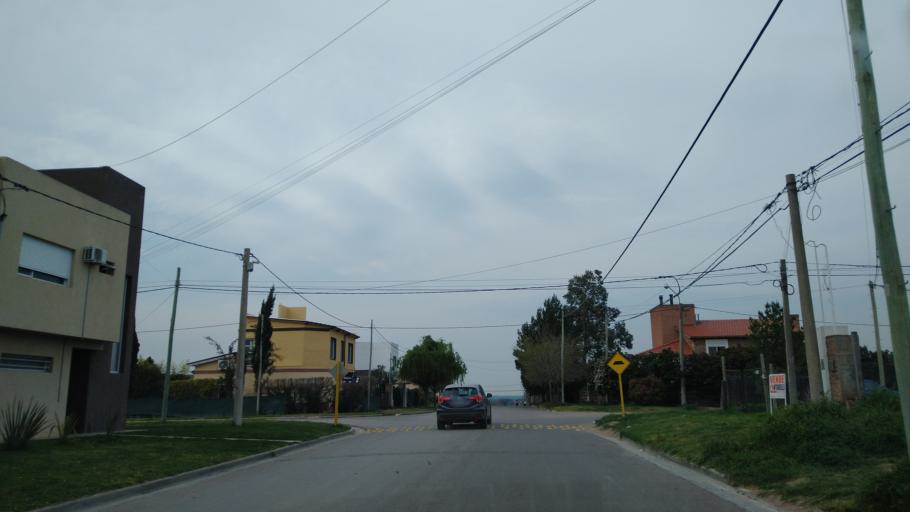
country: AR
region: Buenos Aires
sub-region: Partido de Bahia Blanca
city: Bahia Blanca
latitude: -38.6996
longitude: -62.2384
